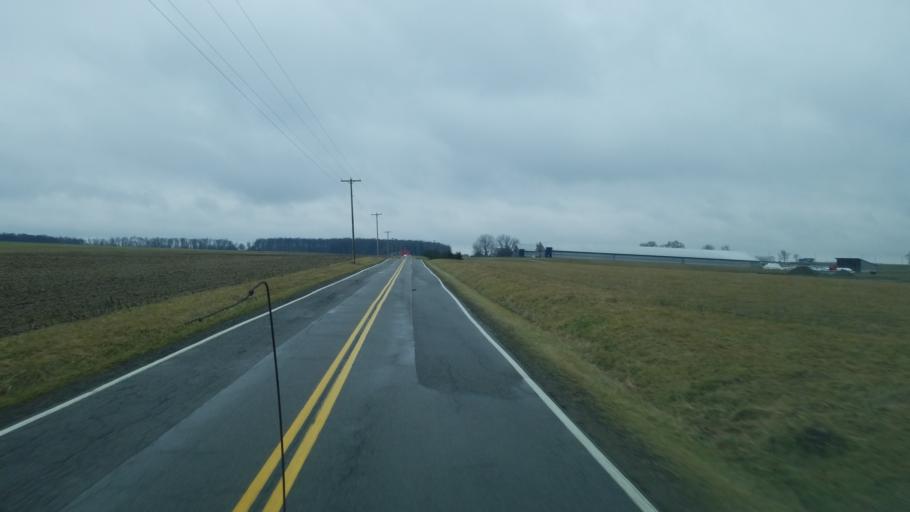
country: US
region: Ohio
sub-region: Wayne County
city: Orrville
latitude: 40.9090
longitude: -81.7824
